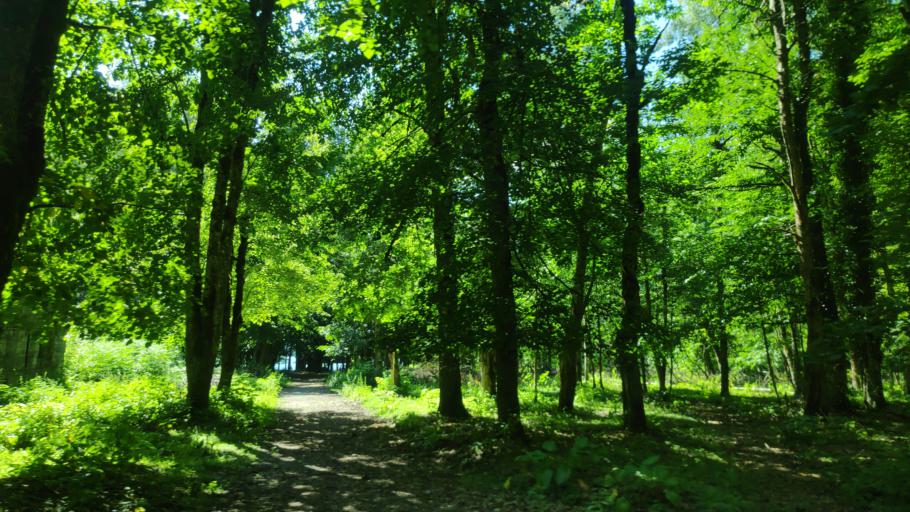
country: GE
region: Abkhazia
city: Gagra
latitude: 43.4803
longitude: 40.5625
